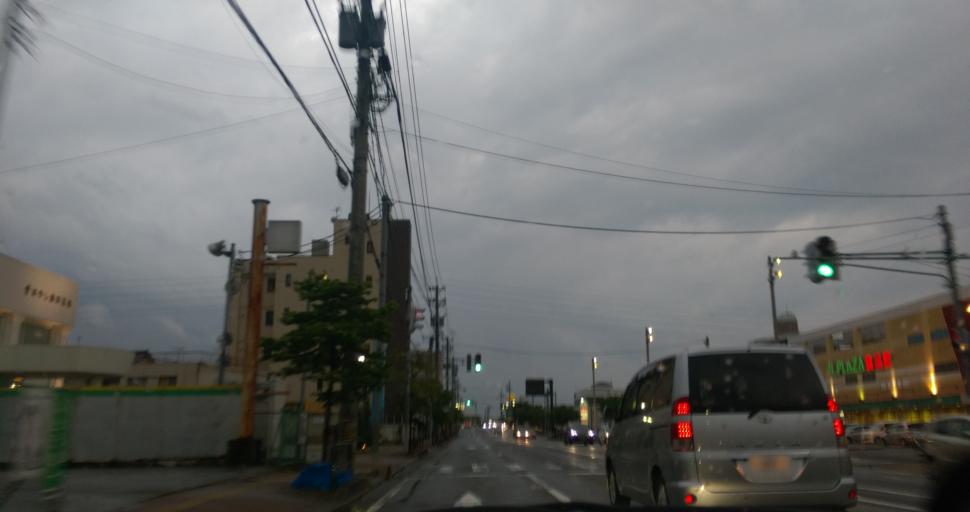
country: JP
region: Fukui
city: Fukui-shi
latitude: 36.0339
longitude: 136.2135
